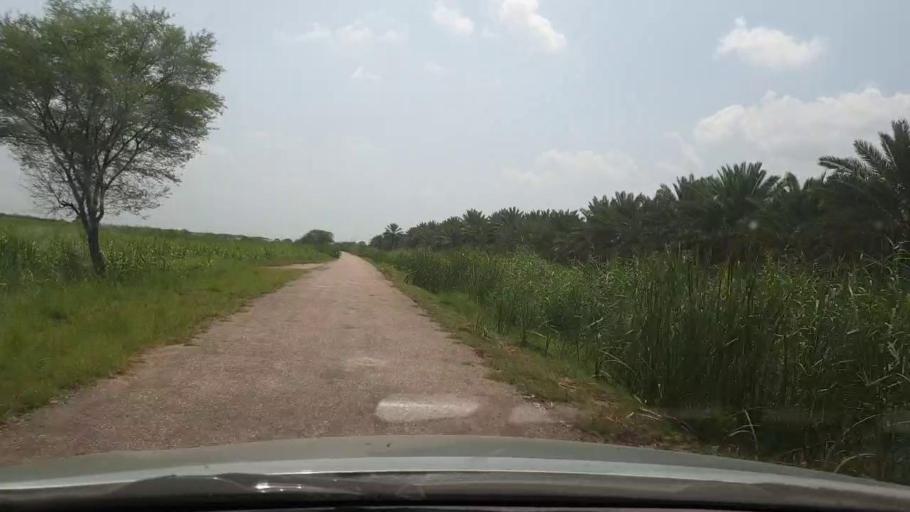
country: PK
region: Sindh
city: Kot Diji
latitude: 27.3936
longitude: 68.7203
